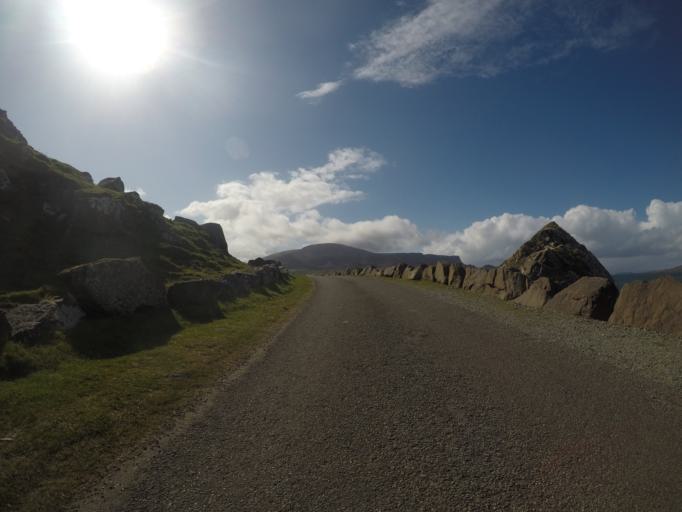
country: GB
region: Scotland
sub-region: Highland
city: Portree
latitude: 57.6369
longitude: -6.2063
